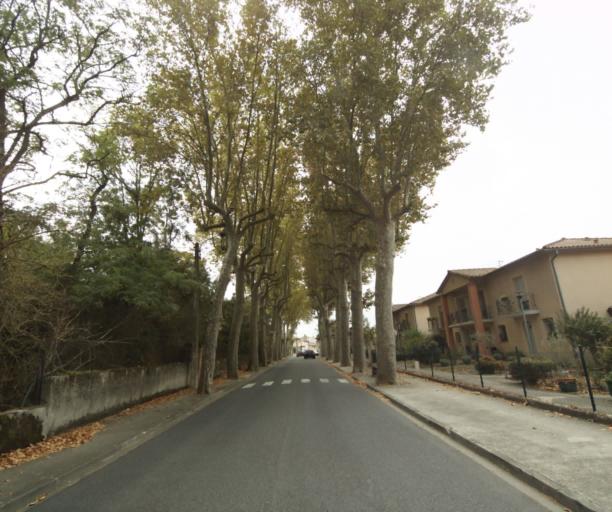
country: FR
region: Midi-Pyrenees
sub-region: Departement de la Haute-Garonne
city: Villefranche-de-Lauragais
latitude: 43.4034
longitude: 1.7167
